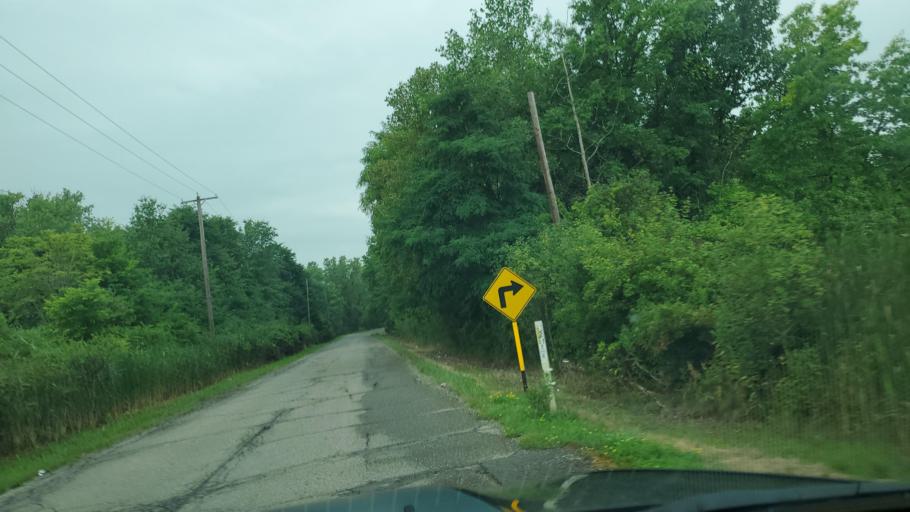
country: US
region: Ohio
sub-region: Trumbull County
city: Warren
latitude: 41.2544
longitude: -80.8052
